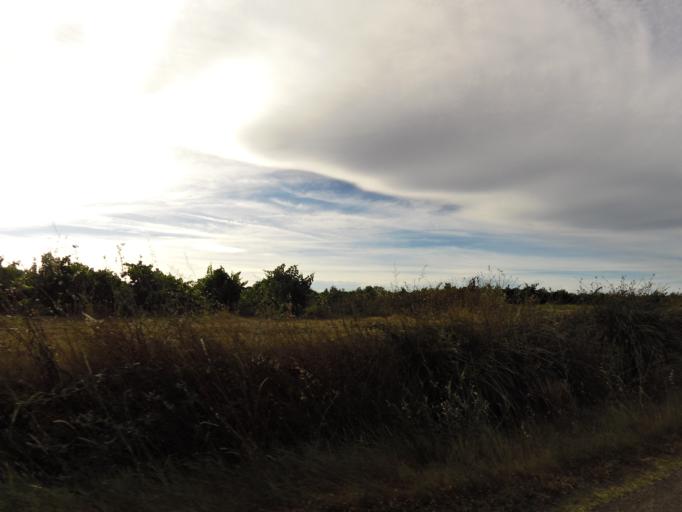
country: FR
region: Languedoc-Roussillon
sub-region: Departement du Gard
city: Saint-Mamert-du-Gard
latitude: 43.8635
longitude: 4.1616
